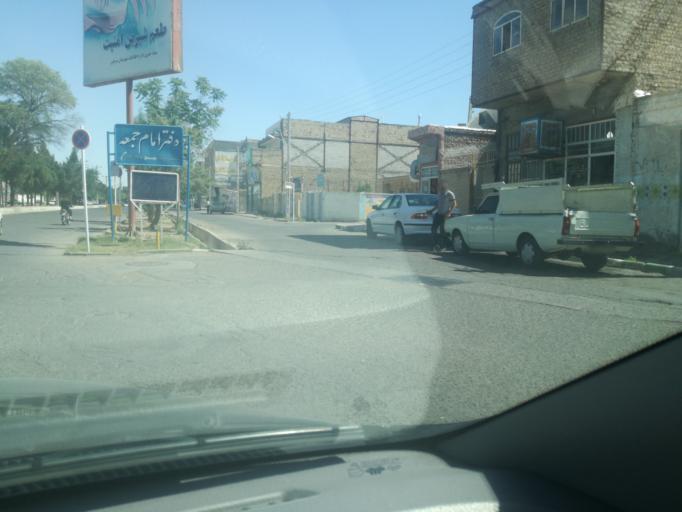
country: IR
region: Razavi Khorasan
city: Sarakhs
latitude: 36.5426
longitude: 61.1641
